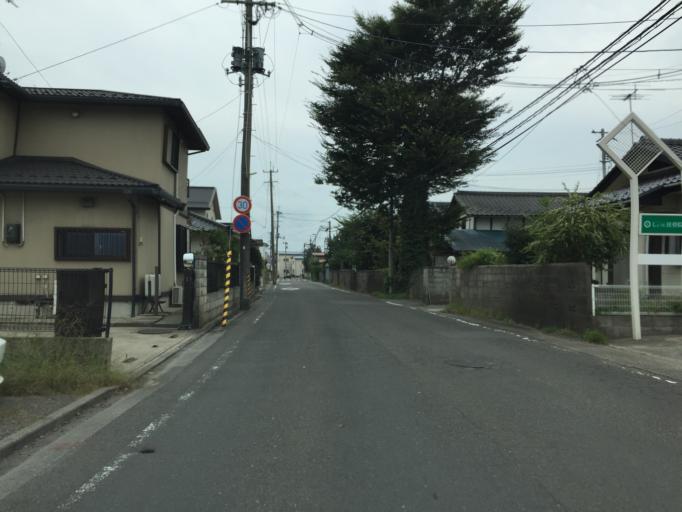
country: JP
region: Fukushima
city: Fukushima-shi
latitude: 37.7693
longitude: 140.4282
